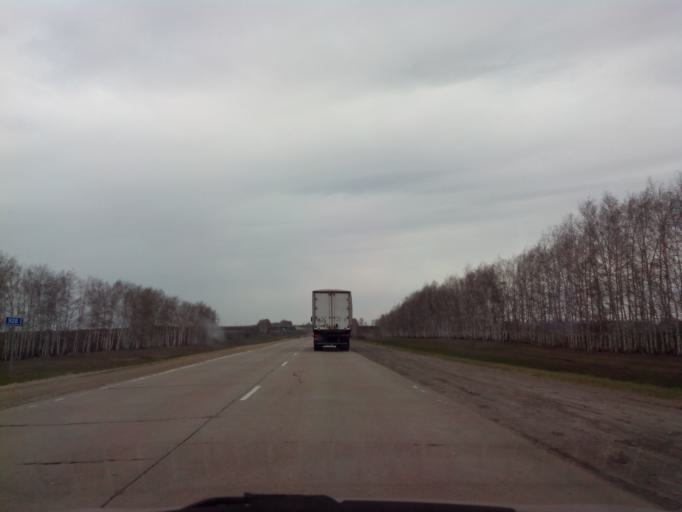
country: RU
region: Tambov
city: Pokrovo-Prigorodnoye
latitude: 52.6523
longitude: 41.3406
